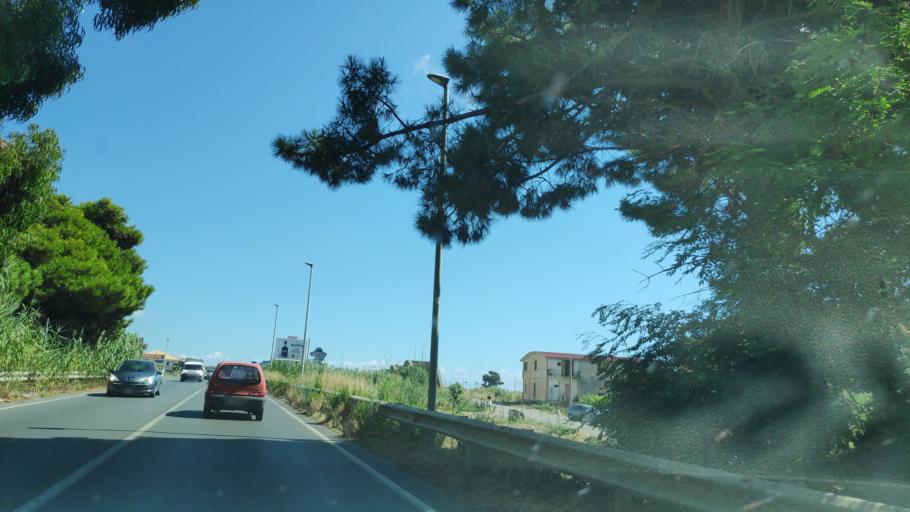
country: IT
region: Calabria
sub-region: Provincia di Cosenza
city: Campora San Giovanni
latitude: 39.0794
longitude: 16.0885
